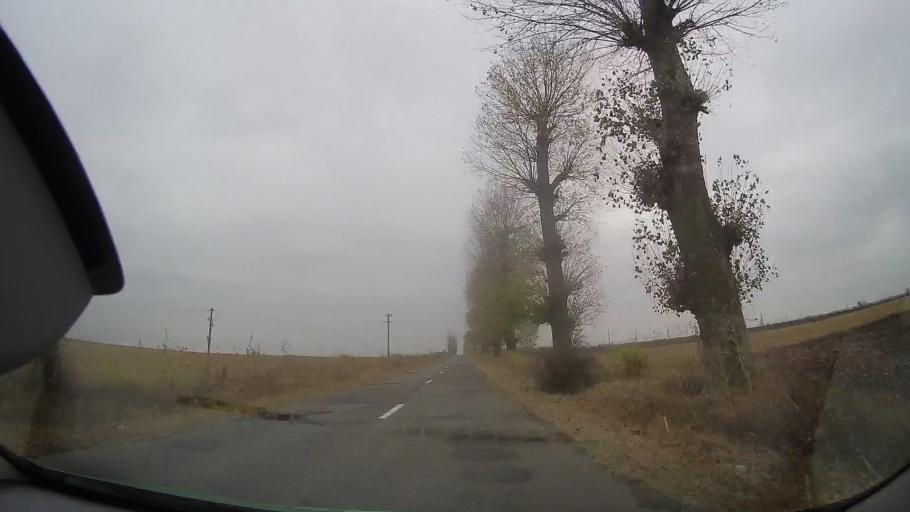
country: RO
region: Ialomita
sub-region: Comuna Valea Macrisului
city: Valea Macrisului
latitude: 44.7479
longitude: 26.8689
